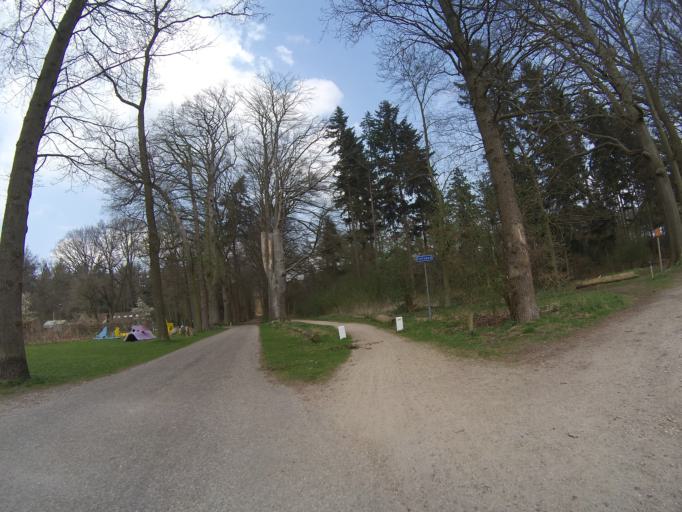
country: NL
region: Utrecht
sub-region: Gemeente Baarn
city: Baarn
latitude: 52.2042
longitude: 5.2357
